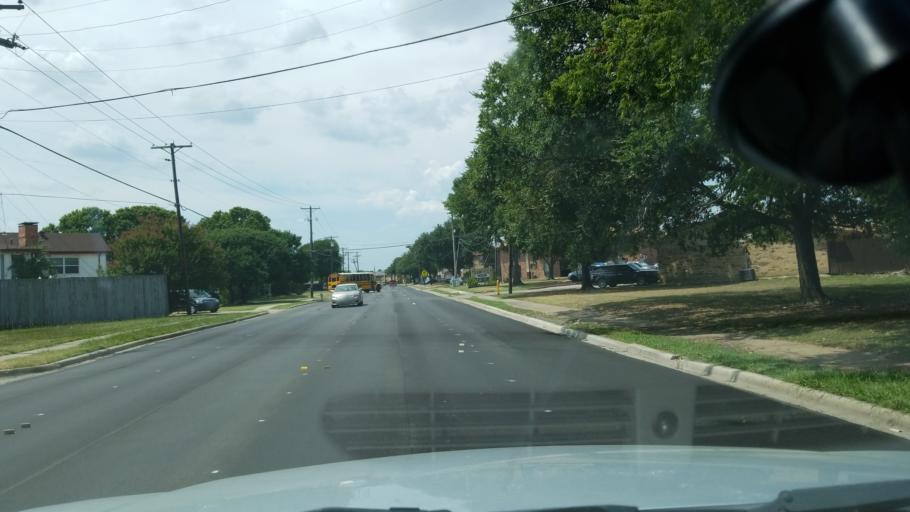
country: US
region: Texas
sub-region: Dallas County
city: Irving
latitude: 32.8258
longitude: -96.9815
